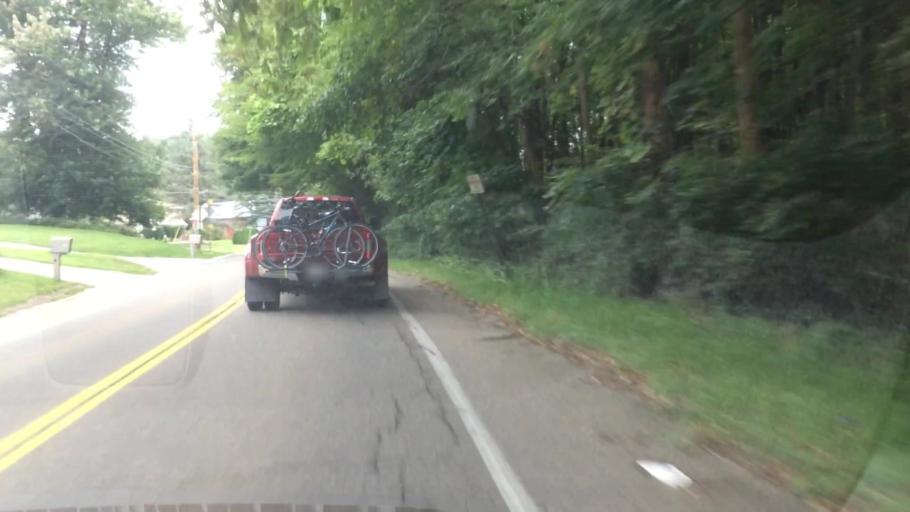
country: US
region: Ohio
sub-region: Summit County
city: Cuyahoga Falls
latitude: 41.1279
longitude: -81.5242
